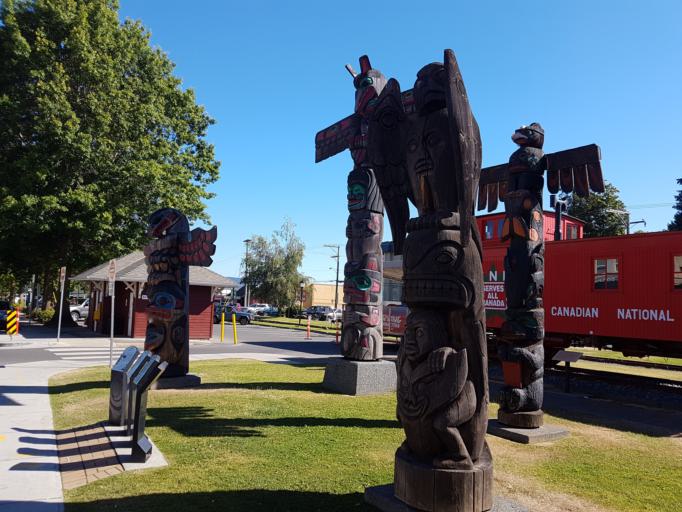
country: CA
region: British Columbia
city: Duncan
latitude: 48.7781
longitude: -123.7070
